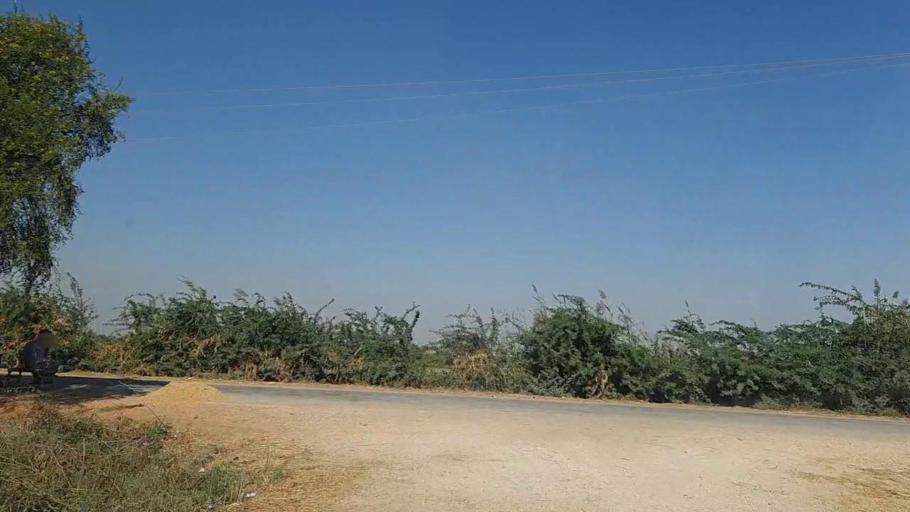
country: PK
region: Sindh
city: Daro Mehar
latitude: 24.7939
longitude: 68.1725
